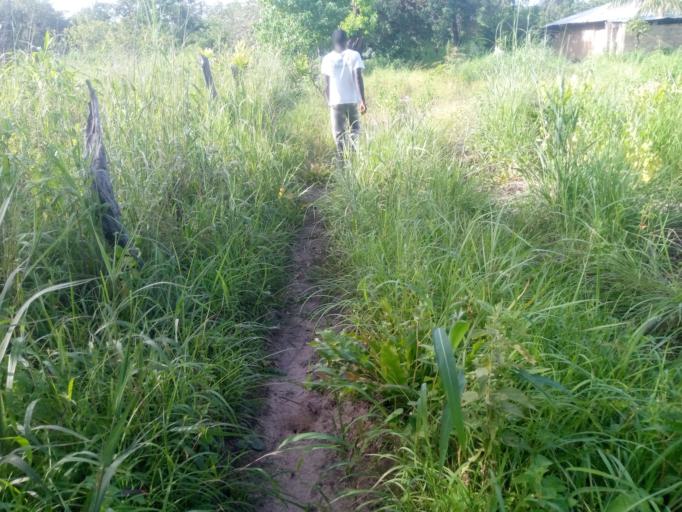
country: GM
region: Western
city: Gunjur
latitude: 13.0340
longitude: -16.7262
